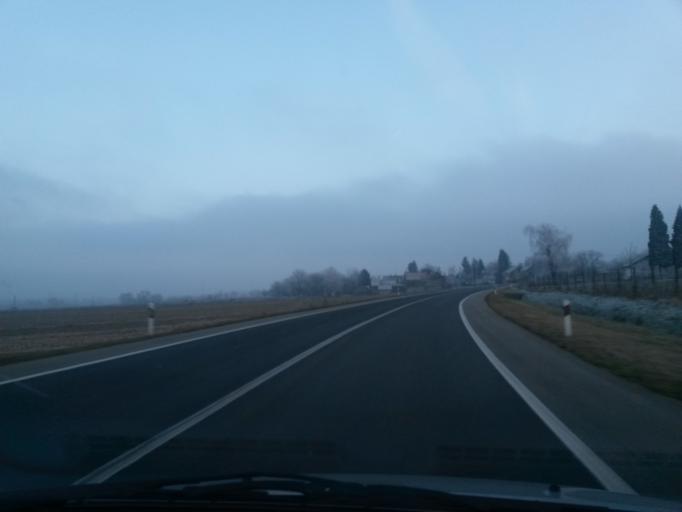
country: HR
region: Varazdinska
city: Ludbreg
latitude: 46.2135
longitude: 16.6923
